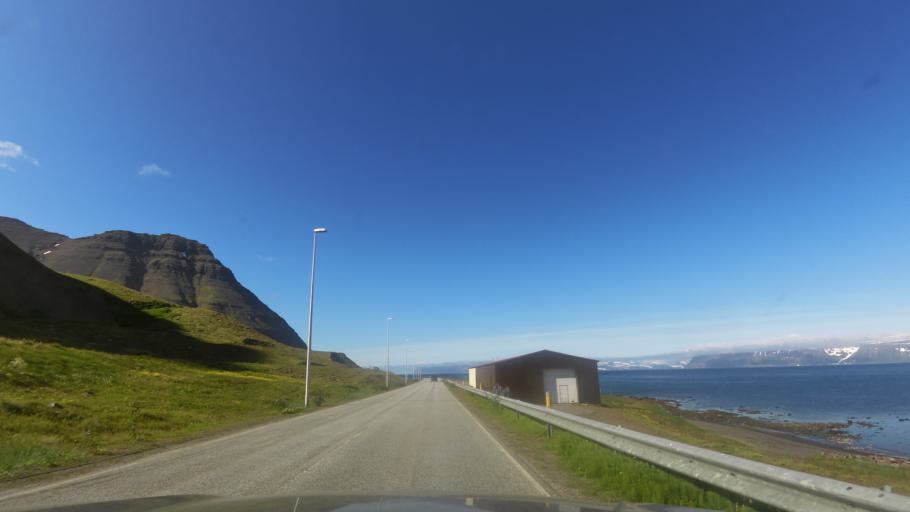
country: IS
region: Westfjords
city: Isafjoerdur
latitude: 66.1040
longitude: -23.1099
